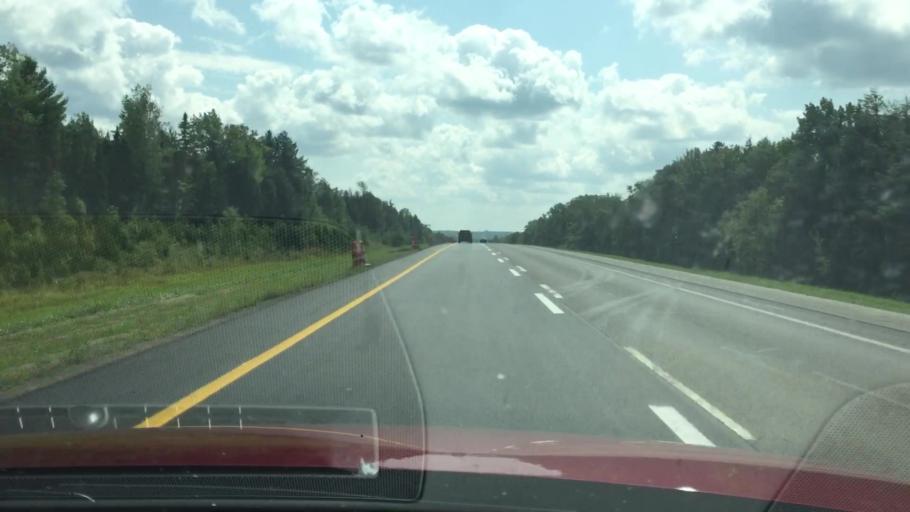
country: US
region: Maine
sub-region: Penobscot County
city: Medway
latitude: 45.6595
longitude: -68.4995
